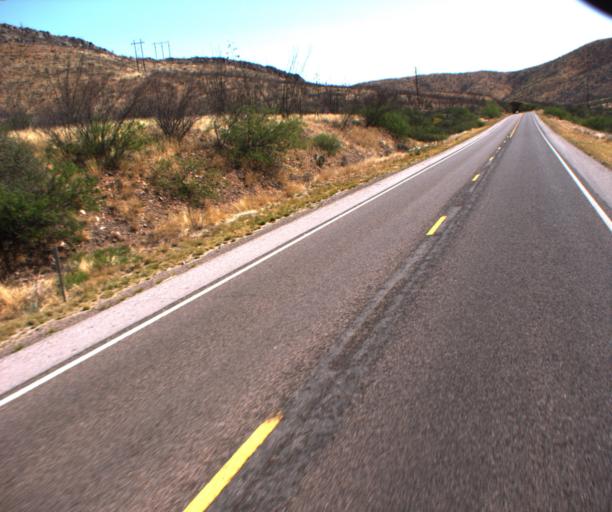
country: US
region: Arizona
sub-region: Cochise County
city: Bisbee
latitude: 31.4324
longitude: -109.8484
